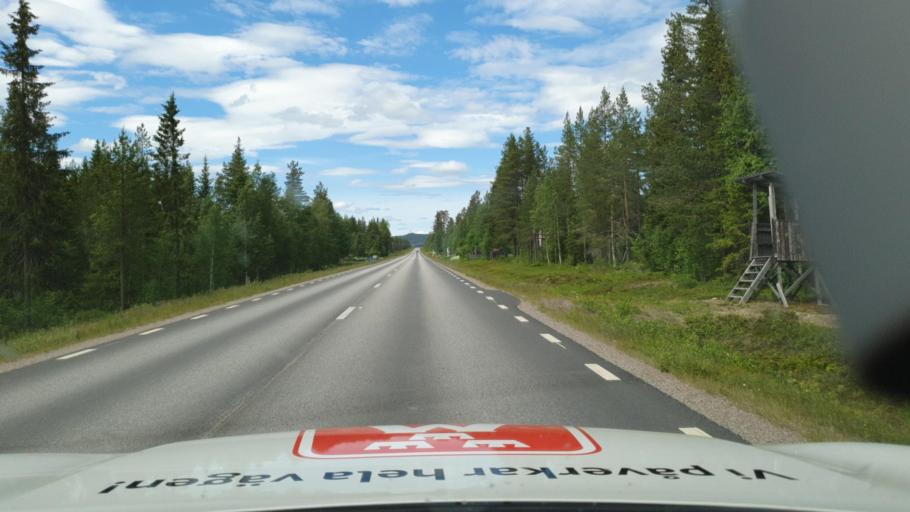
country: SE
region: Vaesterbotten
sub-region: Norsjo Kommun
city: Norsjoe
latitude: 65.2361
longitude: 19.7251
